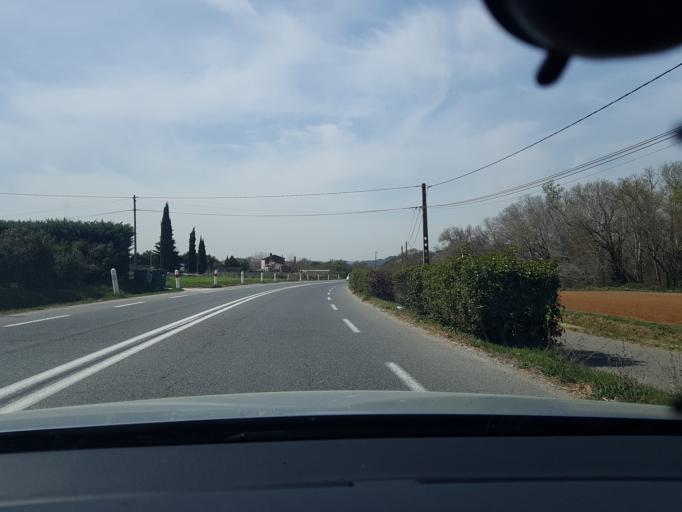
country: FR
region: Provence-Alpes-Cote d'Azur
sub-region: Departement des Bouches-du-Rhone
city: Chateauneuf-le-Rouge
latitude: 43.4728
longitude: 5.5789
